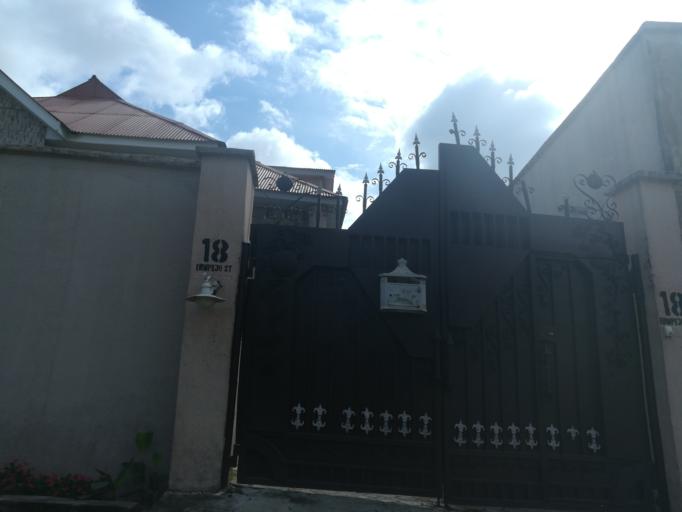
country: NG
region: Lagos
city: Somolu
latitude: 6.5484
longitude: 3.3719
